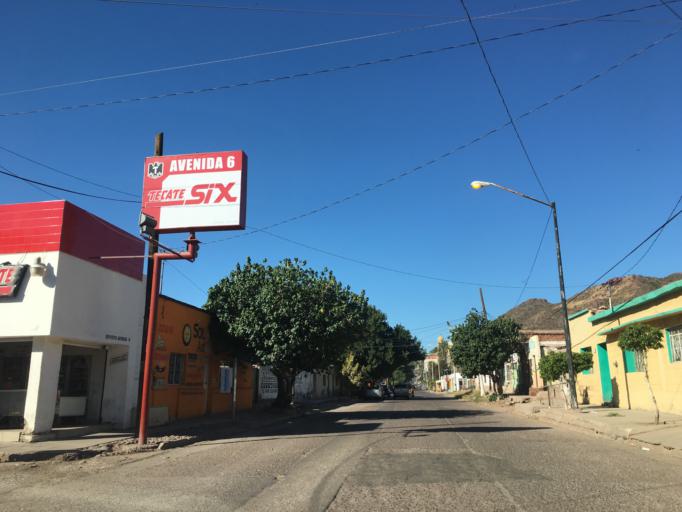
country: MX
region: Sonora
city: Heroica Guaymas
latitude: 27.9183
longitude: -110.8976
